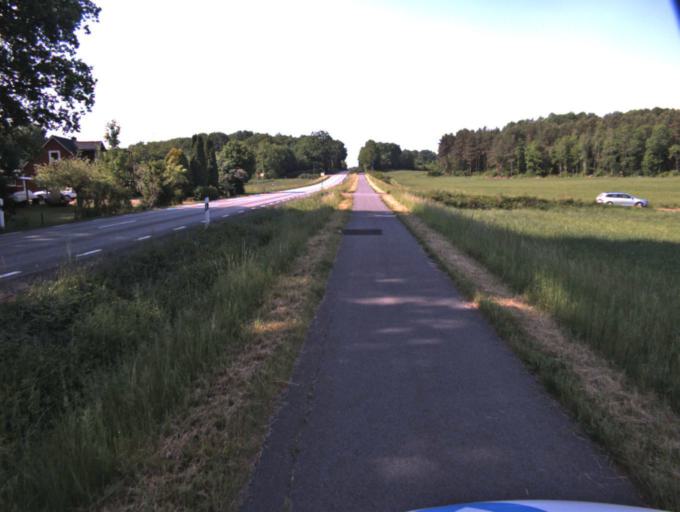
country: SE
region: Skane
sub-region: Kristianstads Kommun
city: Tollarp
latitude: 56.1595
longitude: 14.2719
